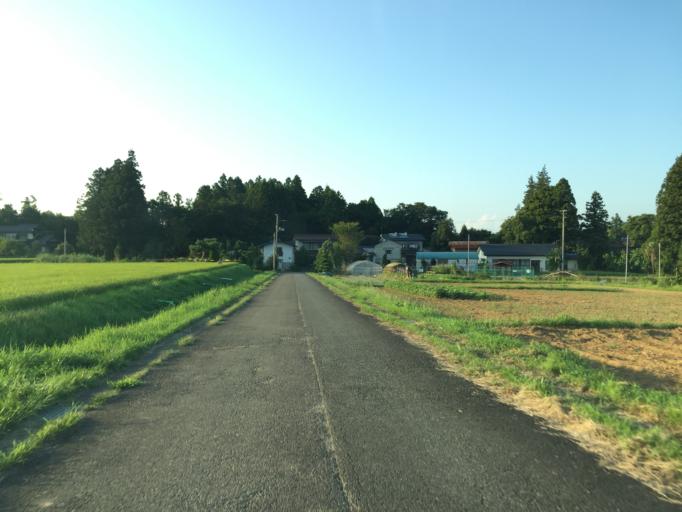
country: JP
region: Fukushima
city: Fukushima-shi
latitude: 37.7290
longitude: 140.3796
